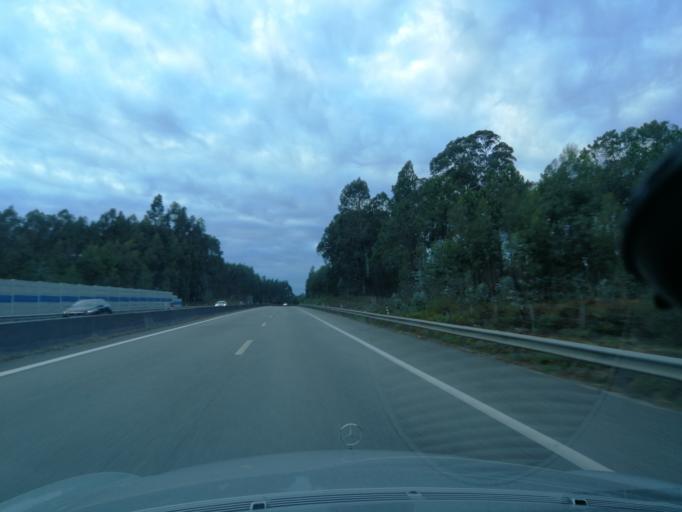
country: PT
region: Aveiro
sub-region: Albergaria-A-Velha
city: Albergaria-a-Velha
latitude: 40.6808
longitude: -8.4917
